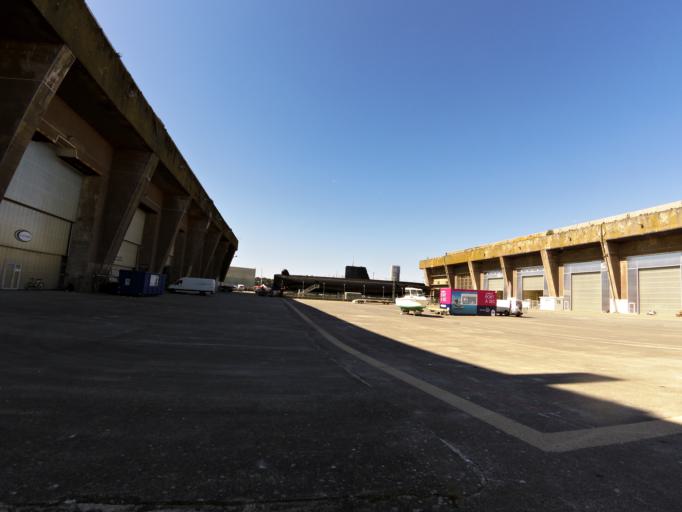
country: FR
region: Brittany
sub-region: Departement du Morbihan
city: Lorient
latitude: 47.7302
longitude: -3.3704
